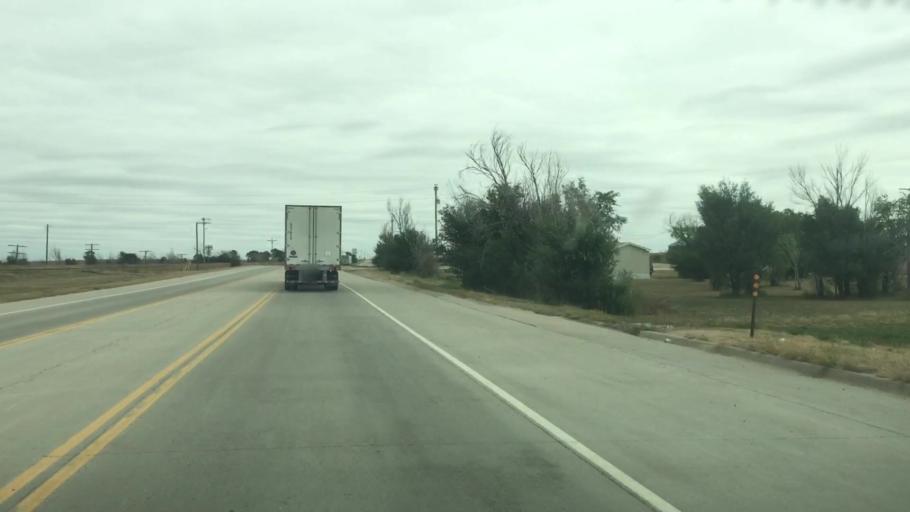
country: US
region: Colorado
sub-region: Kiowa County
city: Eads
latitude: 38.4773
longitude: -102.7738
